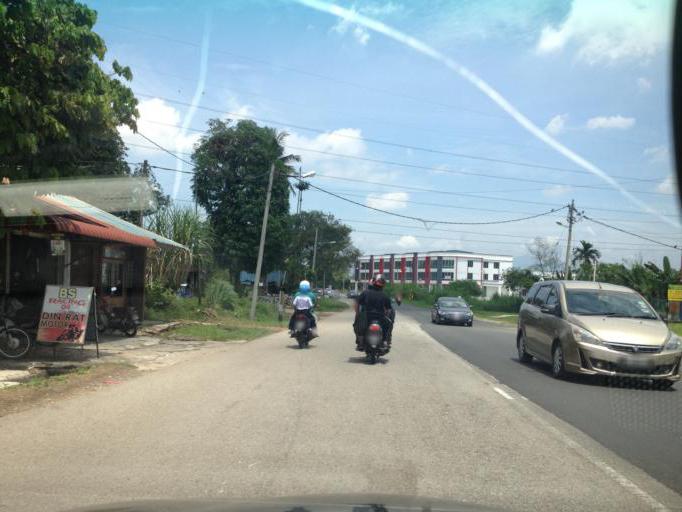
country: MY
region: Kedah
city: Sungai Petani
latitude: 5.6269
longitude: 100.5277
